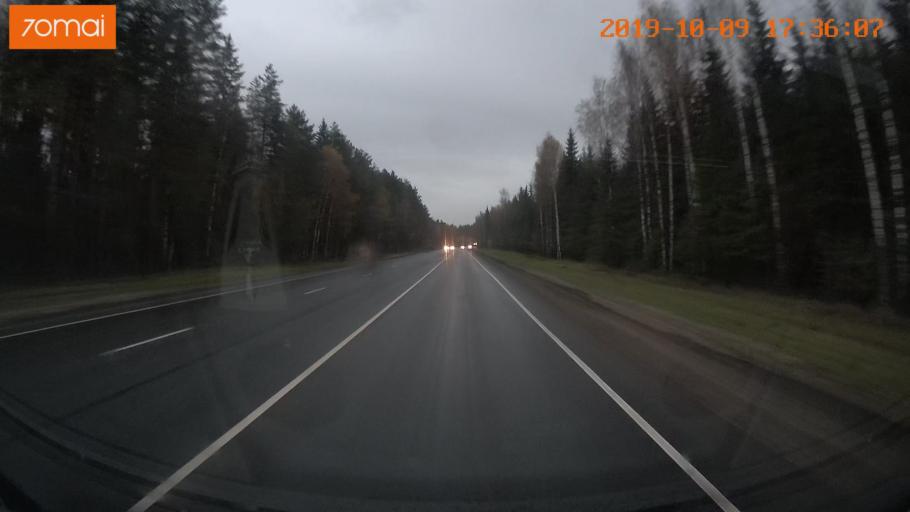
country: RU
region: Ivanovo
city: Bogorodskoye
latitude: 57.0831
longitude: 40.9983
